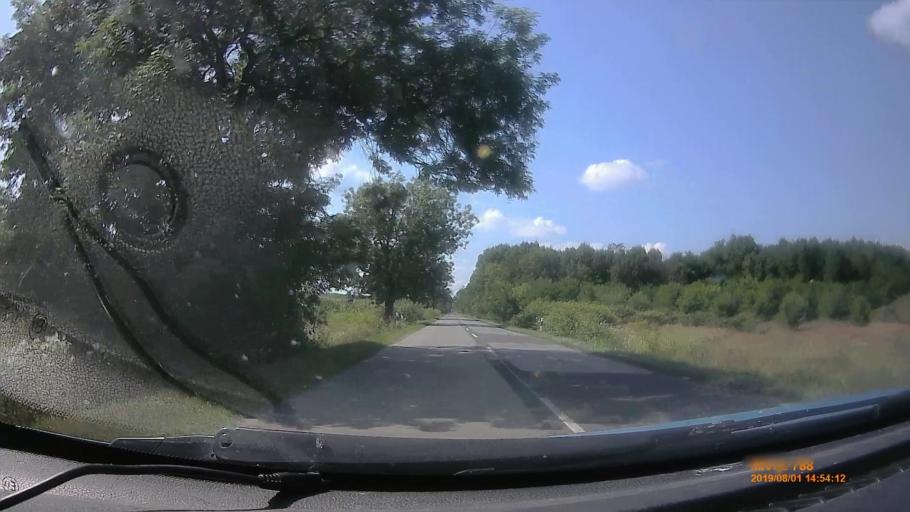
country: HU
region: Baranya
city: Vajszlo
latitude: 45.8638
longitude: 17.9728
